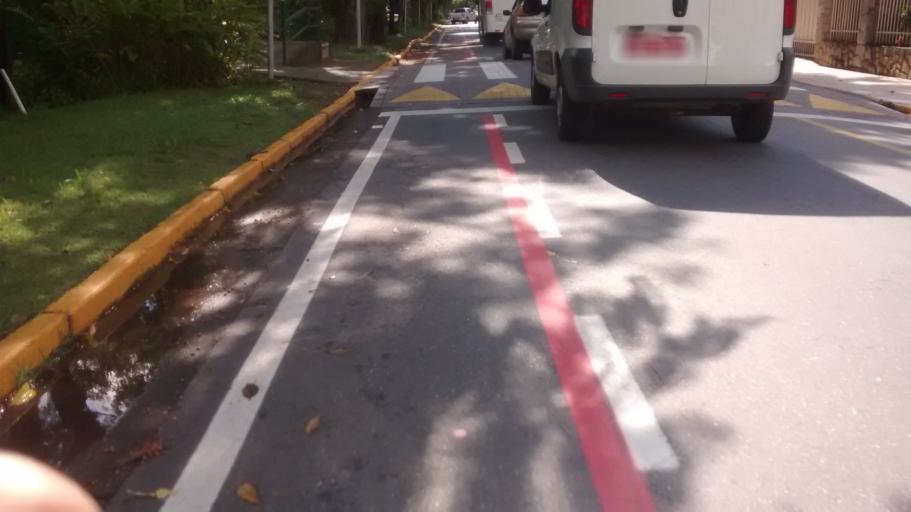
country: BR
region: Minas Gerais
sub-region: Itajuba
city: Itajuba
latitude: -22.4168
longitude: -45.4544
